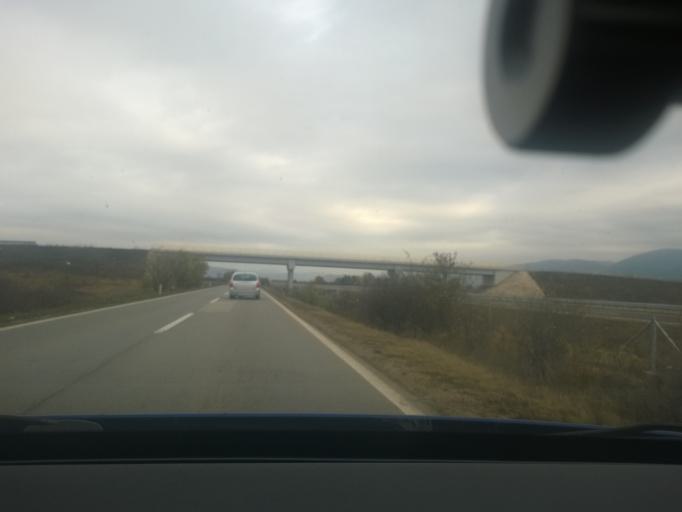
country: RS
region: Central Serbia
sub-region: Pirotski Okrug
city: Pirot
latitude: 43.0943
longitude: 22.6487
